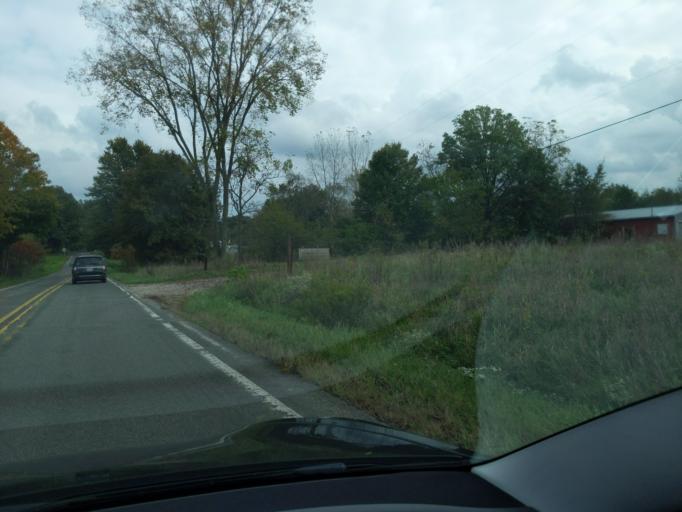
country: US
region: Michigan
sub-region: Ingham County
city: Leslie
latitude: 42.4121
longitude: -84.3832
